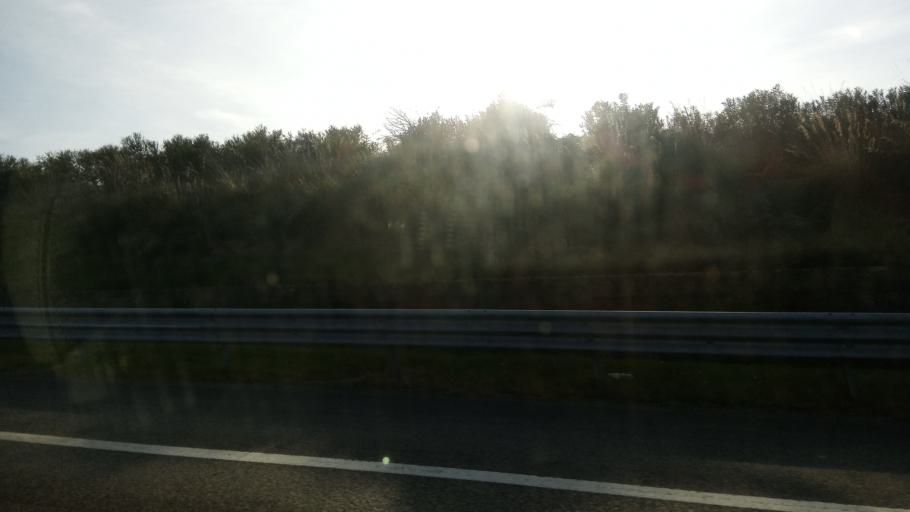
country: IT
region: Molise
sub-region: Provincia di Campobasso
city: Campomarino
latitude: 41.9497
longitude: 15.0225
